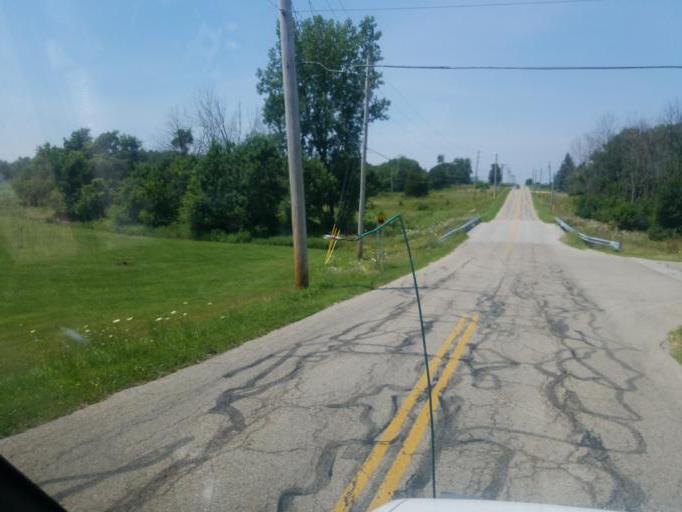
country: US
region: Ohio
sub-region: Logan County
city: De Graff
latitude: 40.3016
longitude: -84.0288
